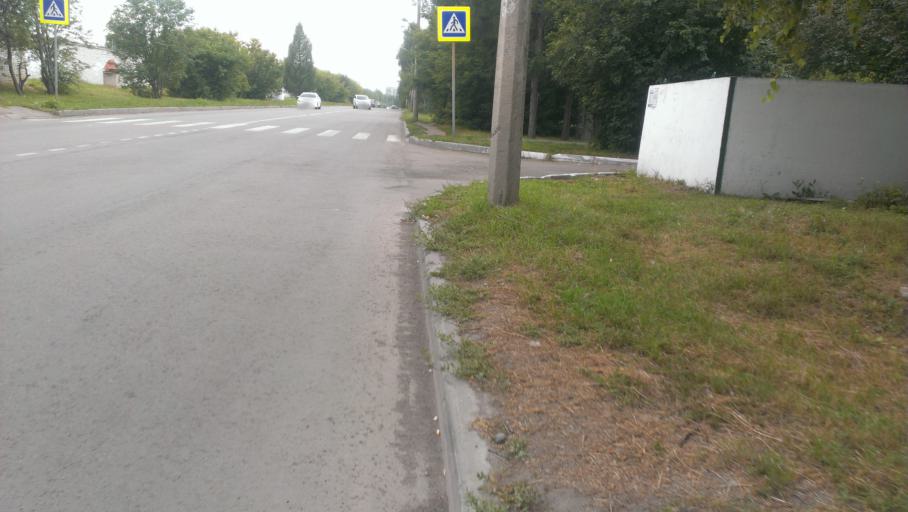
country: RU
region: Altai Krai
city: Yuzhnyy
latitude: 53.2543
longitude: 83.7006
